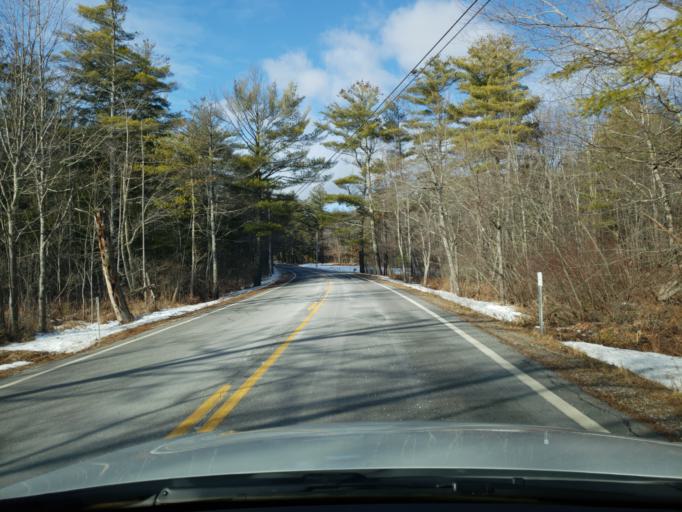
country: US
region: New Hampshire
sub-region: Hillsborough County
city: New Boston
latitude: 42.9983
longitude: -71.7554
